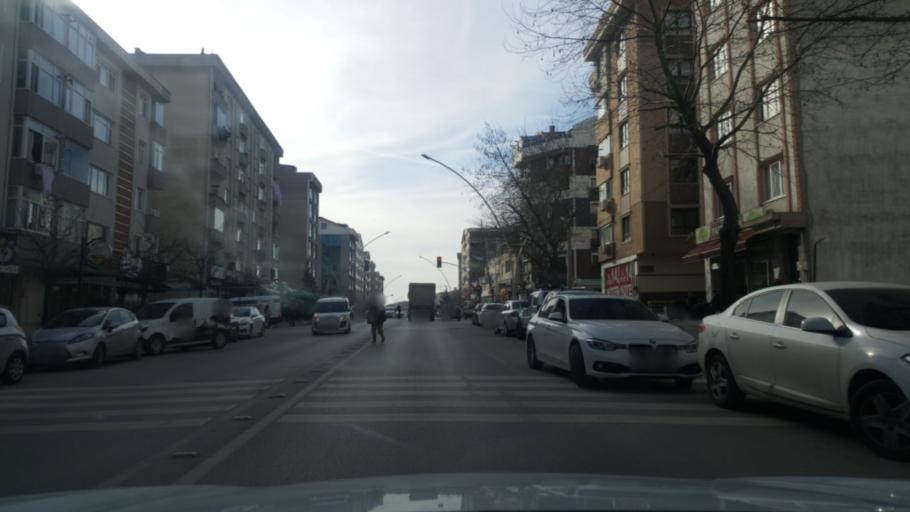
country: TR
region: Kocaeli
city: Gebze
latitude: 40.7918
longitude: 29.4368
